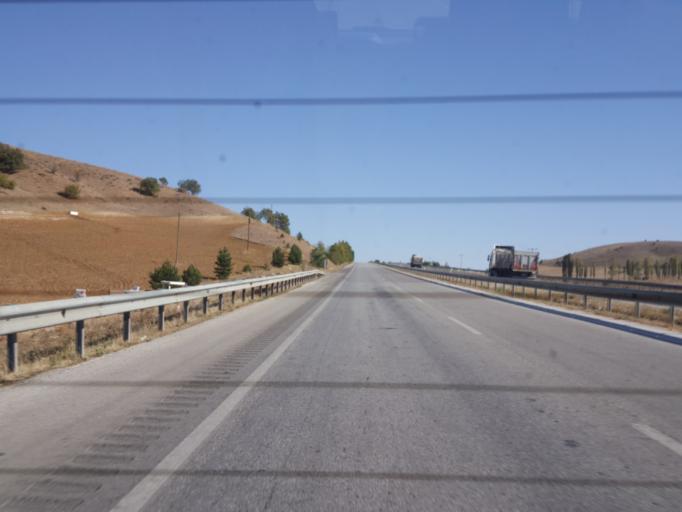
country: TR
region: Corum
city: Alaca
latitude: 40.2837
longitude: 34.6473
